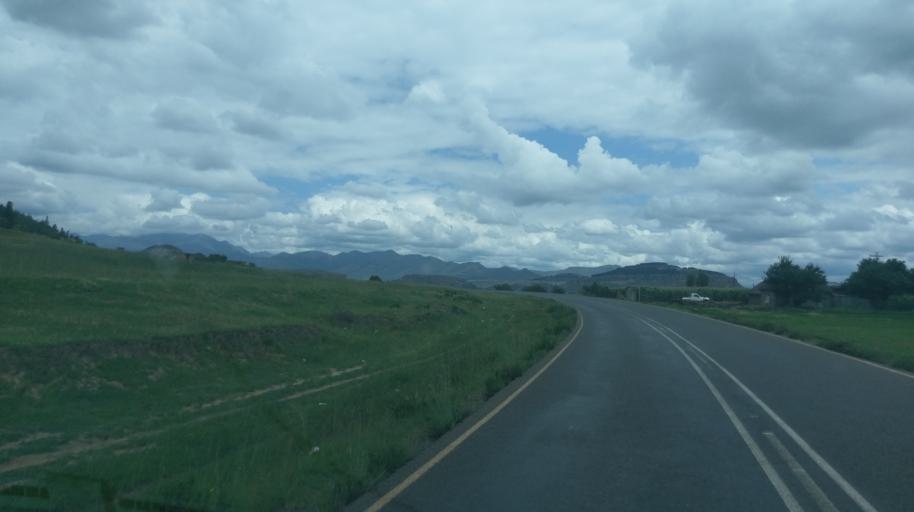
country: LS
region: Leribe
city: Leribe
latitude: -28.9606
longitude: 28.1717
